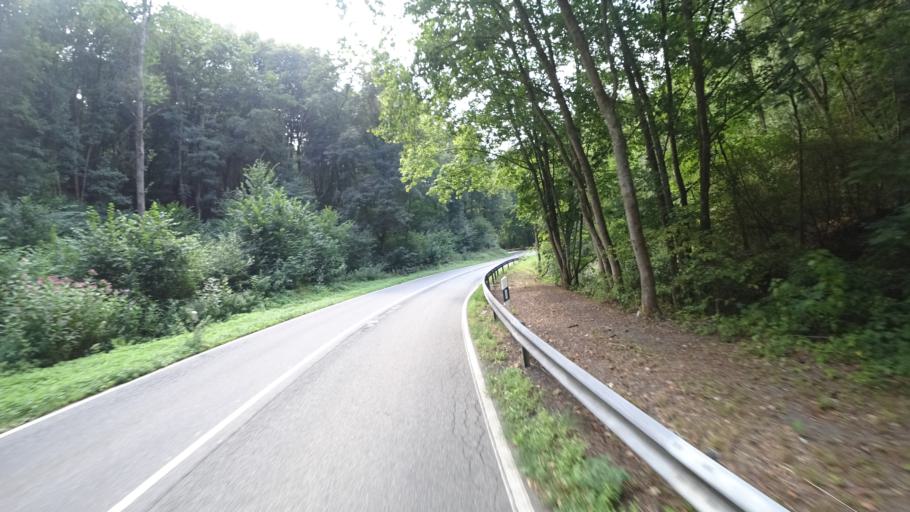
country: DE
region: Rheinland-Pfalz
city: Vallendar
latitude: 50.4157
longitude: 7.6370
